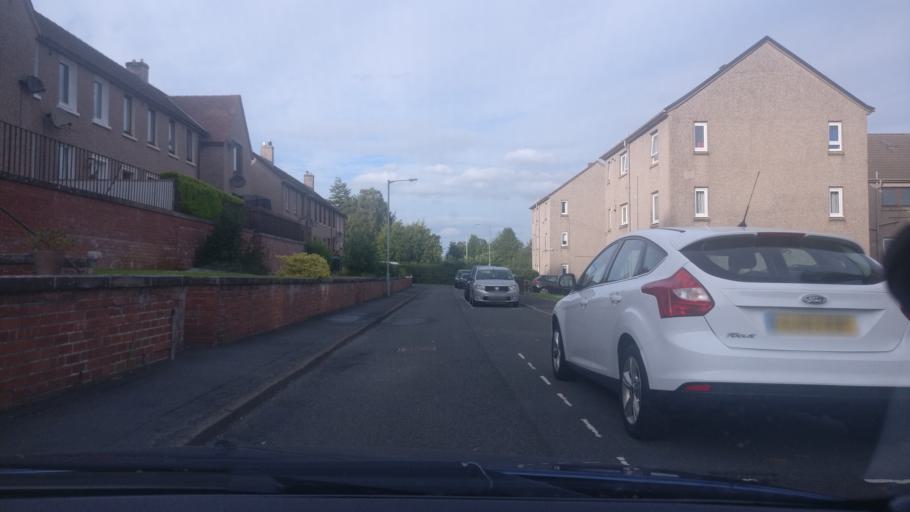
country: GB
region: Scotland
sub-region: The Scottish Borders
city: Hawick
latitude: 55.4344
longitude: -2.7851
